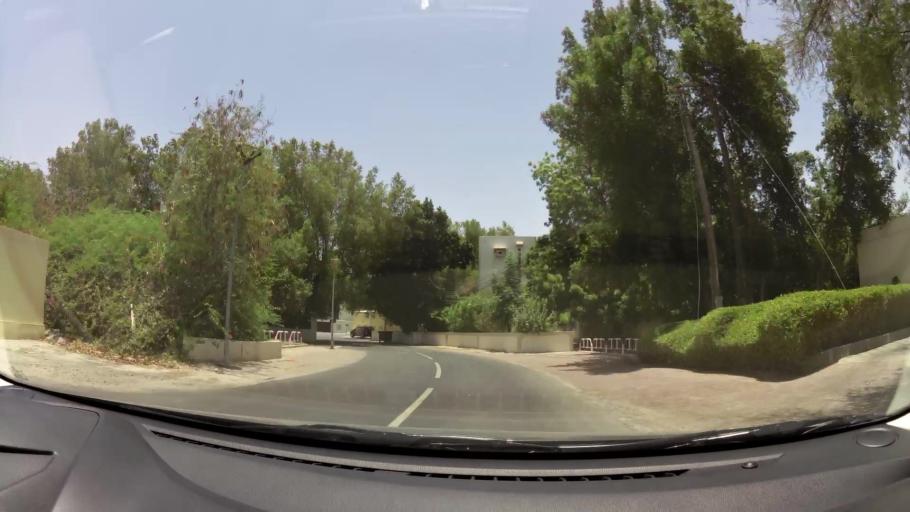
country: OM
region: Muhafazat Masqat
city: Bawshar
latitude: 23.5991
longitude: 58.4592
